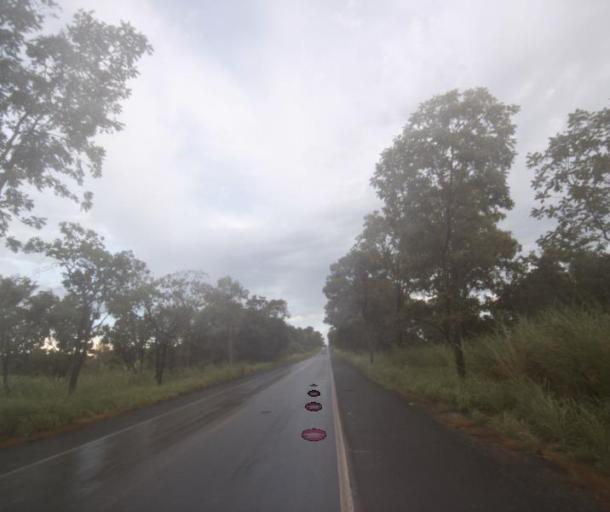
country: BR
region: Goias
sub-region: Porangatu
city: Porangatu
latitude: -13.8041
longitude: -49.0377
